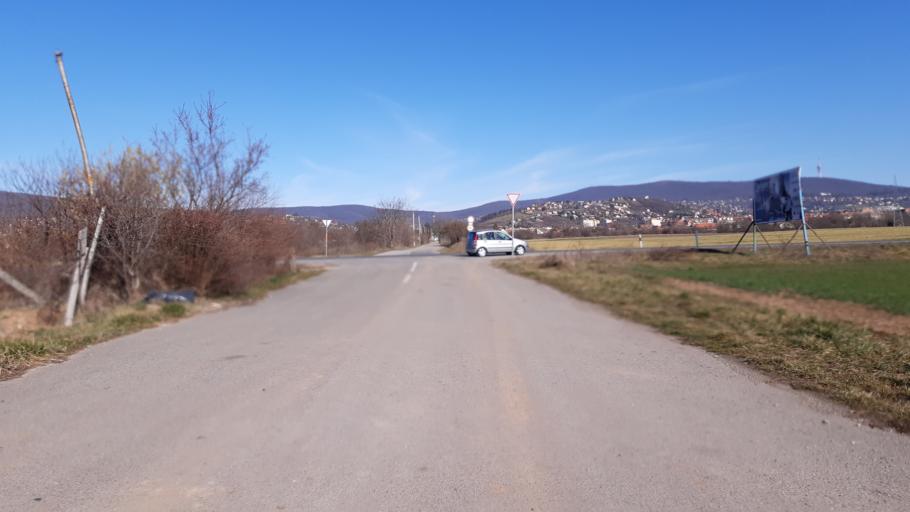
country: HU
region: Baranya
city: Pellerd
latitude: 46.0545
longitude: 18.1878
